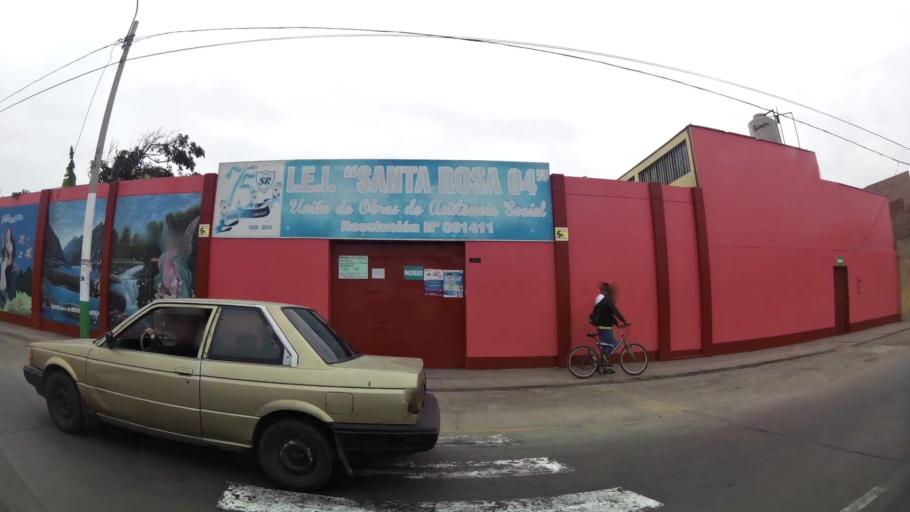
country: PE
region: Callao
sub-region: Callao
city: Callao
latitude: -12.0715
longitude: -77.1228
